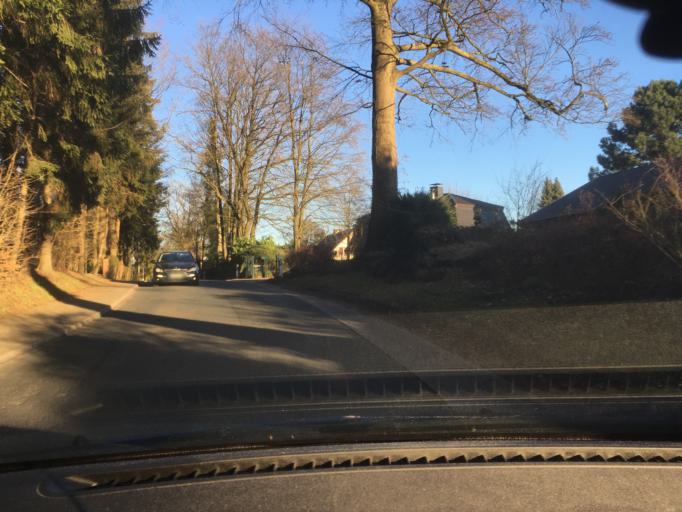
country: DE
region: Lower Saxony
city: Seevetal
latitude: 53.4030
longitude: 9.9281
